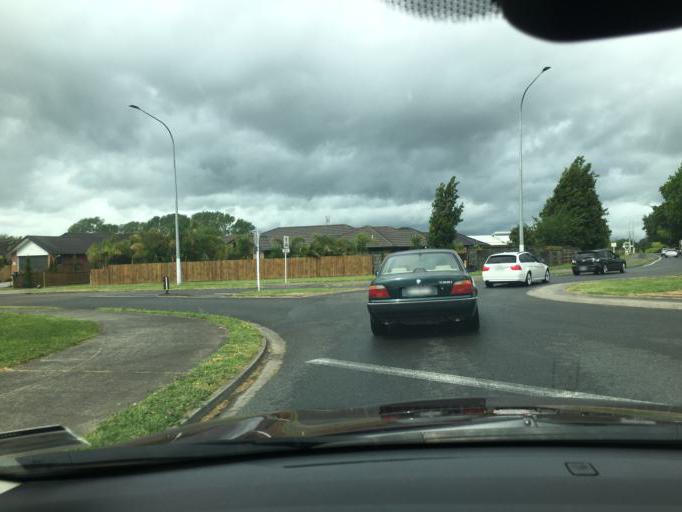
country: NZ
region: Waikato
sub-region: Waipa District
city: Cambridge
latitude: -37.8997
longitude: 175.4621
